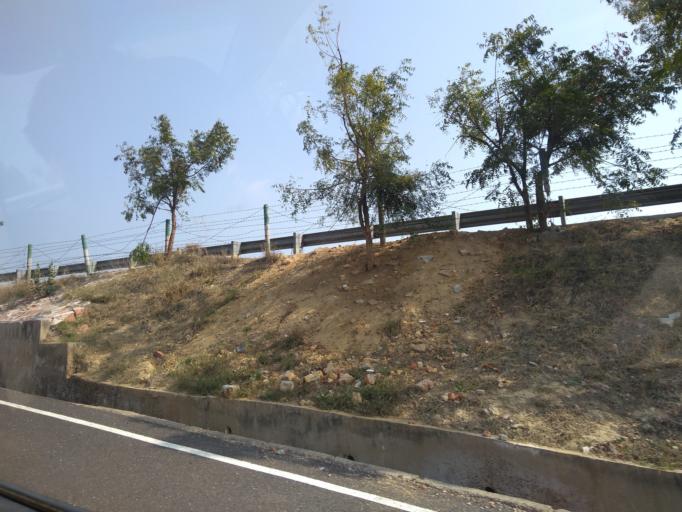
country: IN
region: Uttar Pradesh
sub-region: Mathura
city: Vrindavan
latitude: 27.6129
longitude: 77.7424
